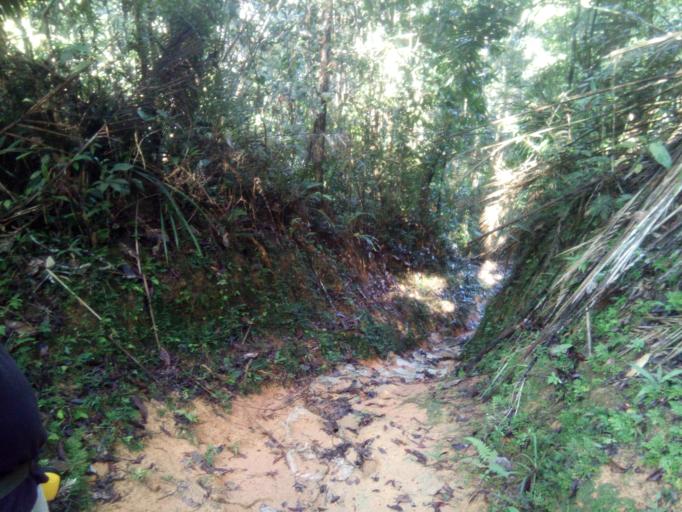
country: MY
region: Penang
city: Tanjung Tokong
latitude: 5.4167
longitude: 100.2582
